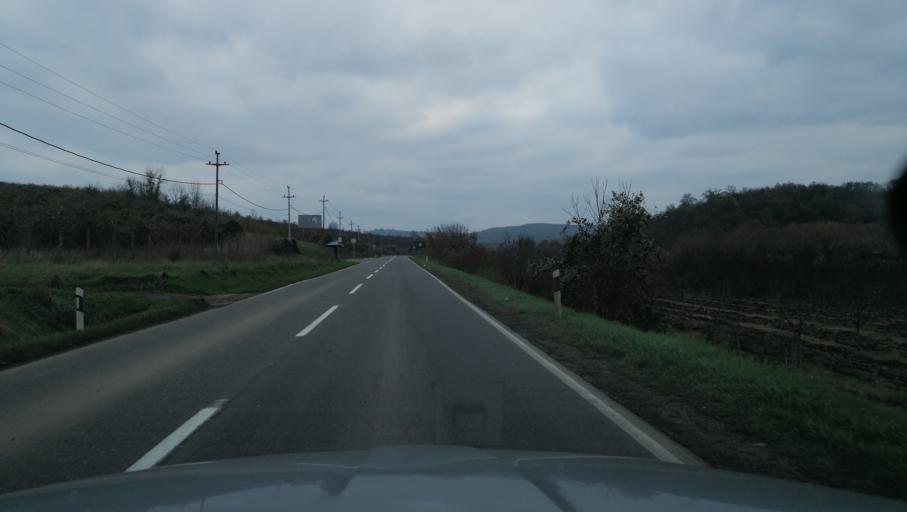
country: RS
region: Central Serbia
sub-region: Belgrade
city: Zvezdara
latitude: 44.7291
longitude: 20.6208
